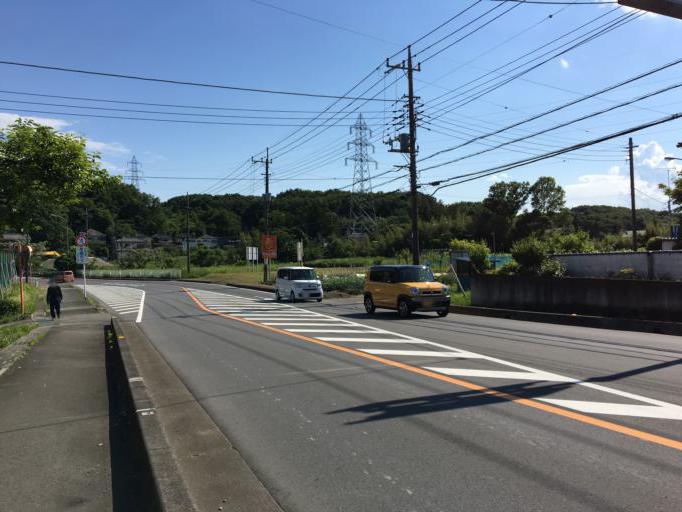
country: JP
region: Saitama
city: Morohongo
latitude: 35.9856
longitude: 139.3322
